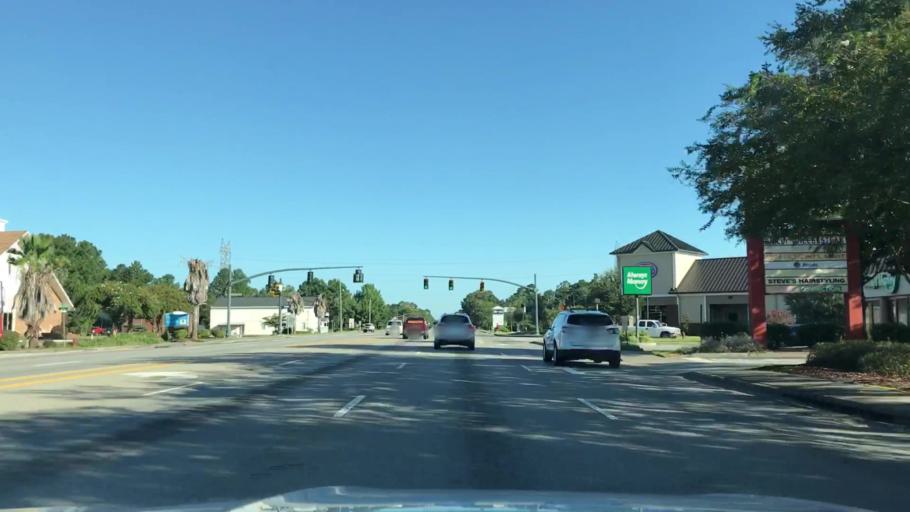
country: US
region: South Carolina
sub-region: Berkeley County
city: Goose Creek
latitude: 33.0012
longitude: -80.0414
